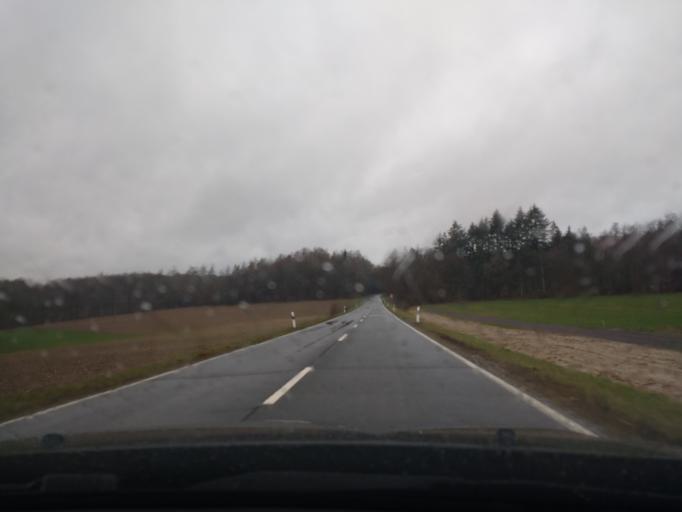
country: DE
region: Rheinland-Pfalz
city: Irmenach
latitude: 49.9324
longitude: 7.1640
